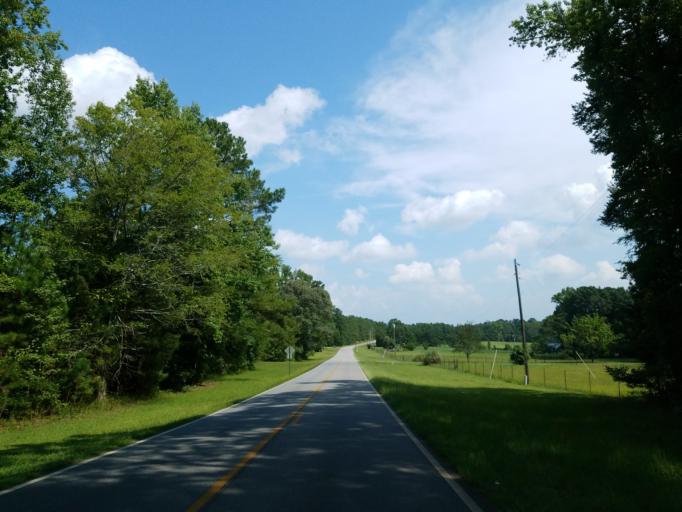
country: US
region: Georgia
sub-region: Monroe County
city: Forsyth
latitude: 33.0107
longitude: -83.8539
